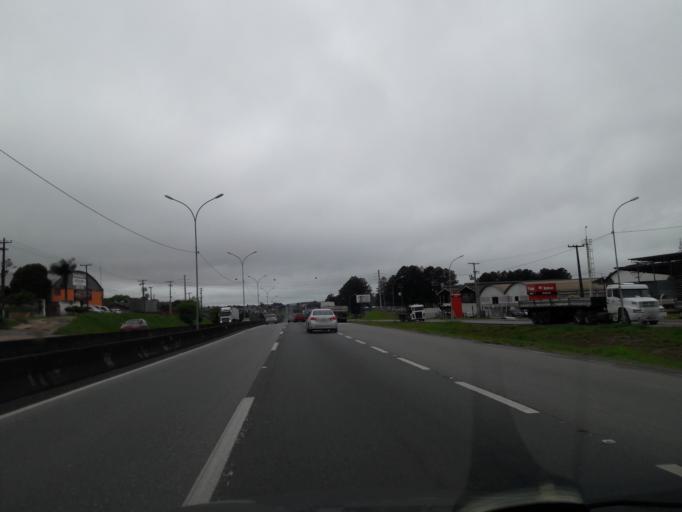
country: BR
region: Parana
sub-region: Quatro Barras
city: Quatro Barras
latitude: -25.3721
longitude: -49.1357
